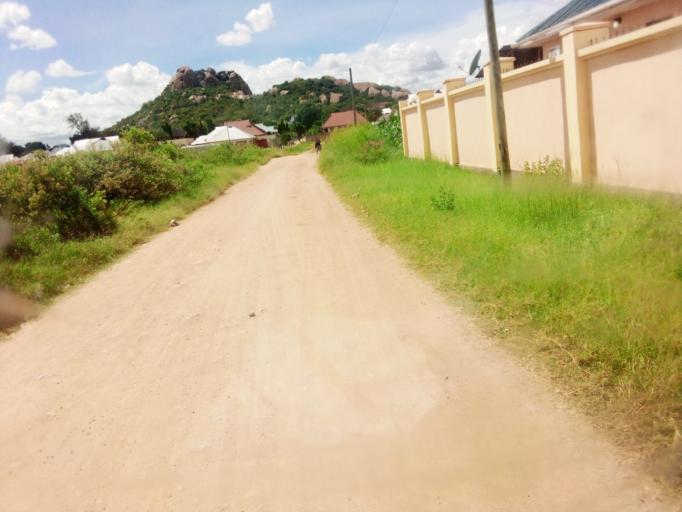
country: TZ
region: Dodoma
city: Dodoma
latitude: -6.1639
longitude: 35.7650
